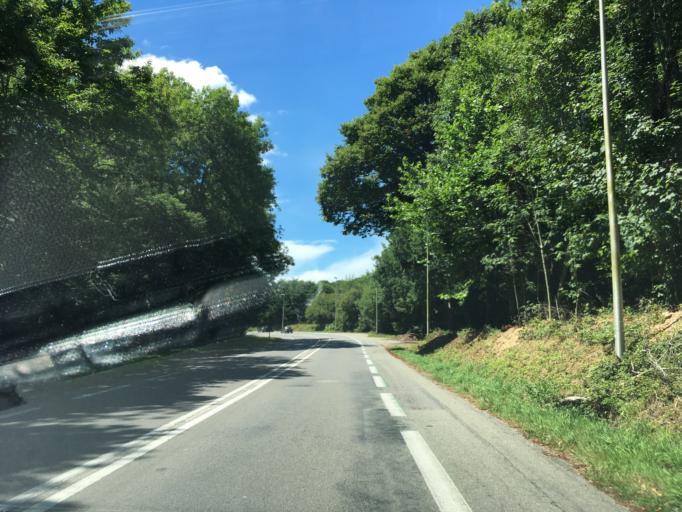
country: FR
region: Brittany
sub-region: Departement du Finistere
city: Quimper
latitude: 47.9764
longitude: -4.0797
